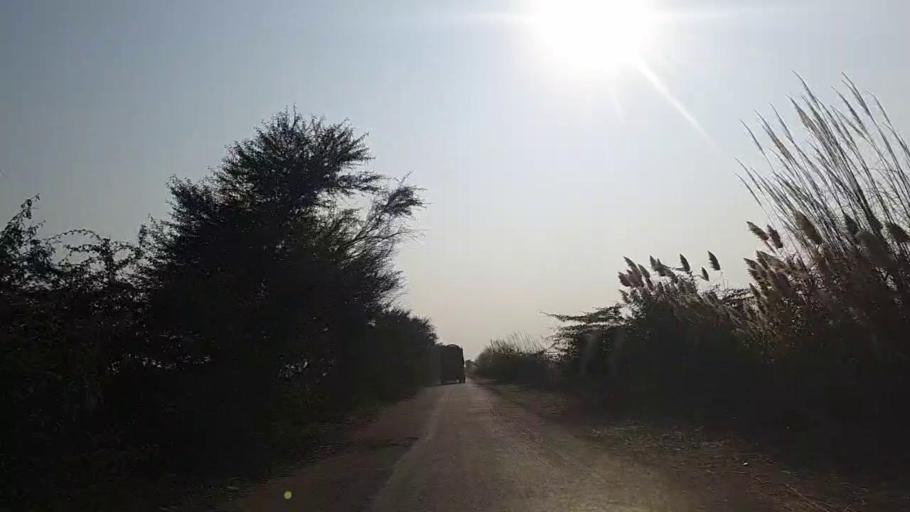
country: PK
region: Sindh
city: Jam Sahib
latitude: 26.2781
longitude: 68.6171
